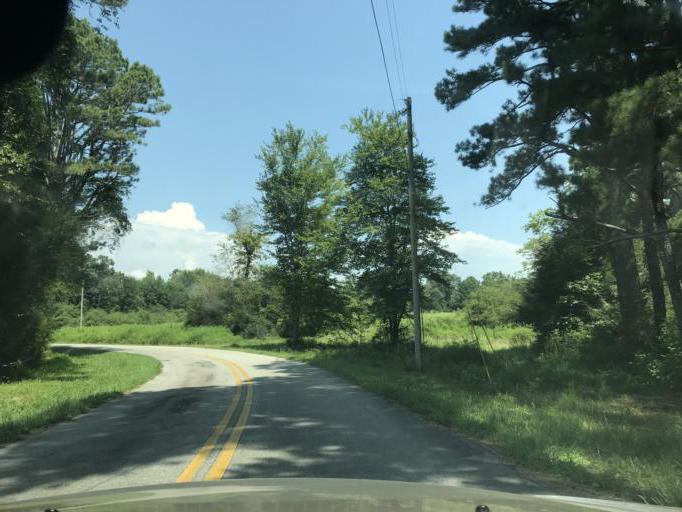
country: US
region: Georgia
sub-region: Dawson County
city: Dawsonville
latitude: 34.3327
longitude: -84.0609
